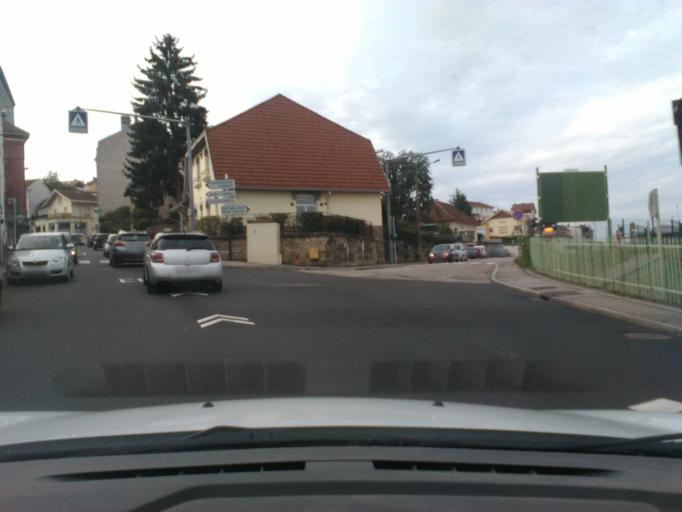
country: FR
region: Lorraine
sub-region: Departement des Vosges
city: Chantraine
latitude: 48.1768
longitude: 6.4411
